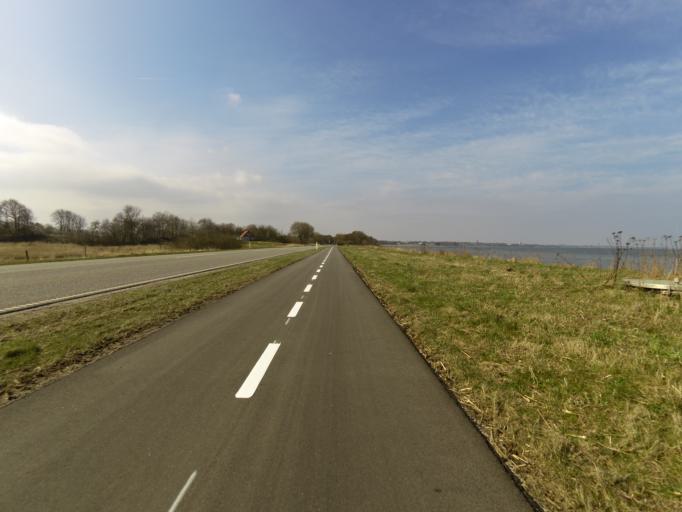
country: DK
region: Central Jutland
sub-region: Struer Kommune
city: Struer
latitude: 56.4689
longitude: 8.6382
